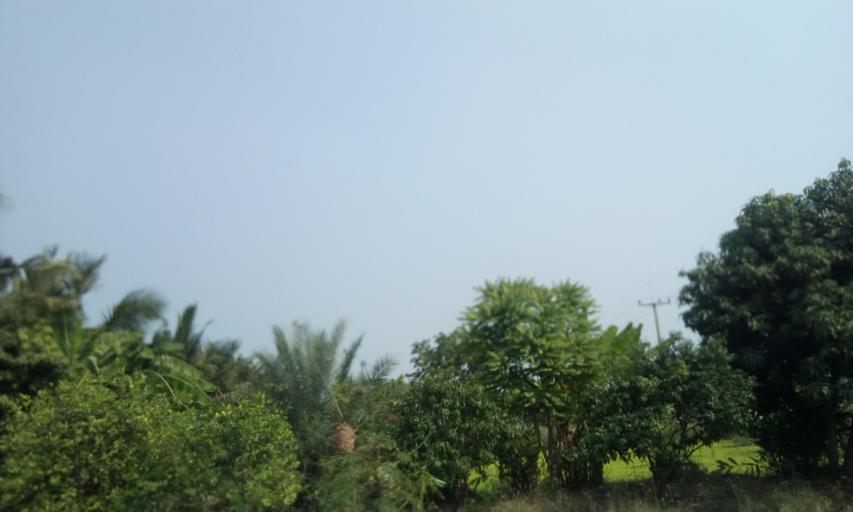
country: TH
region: Pathum Thani
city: Lam Luk Ka
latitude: 13.9492
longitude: 100.7248
